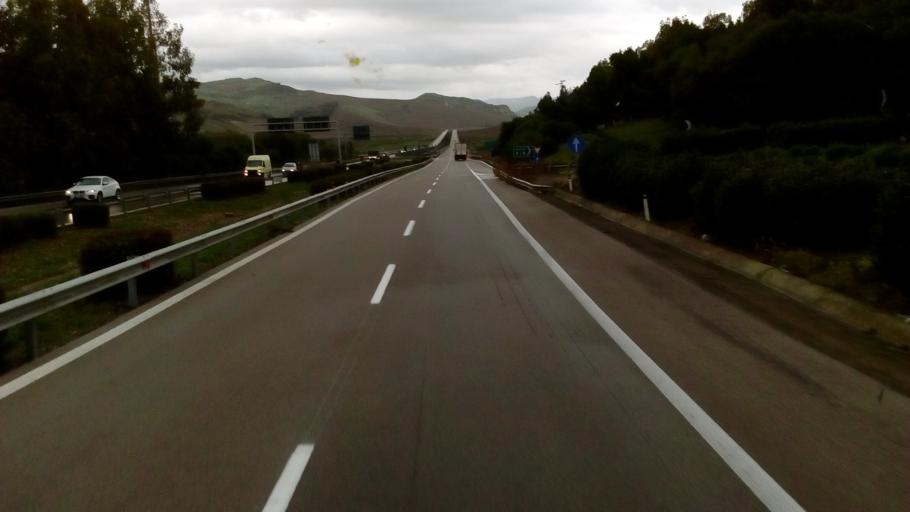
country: IT
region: Sicily
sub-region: Enna
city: Villarosa
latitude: 37.5487
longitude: 14.1430
